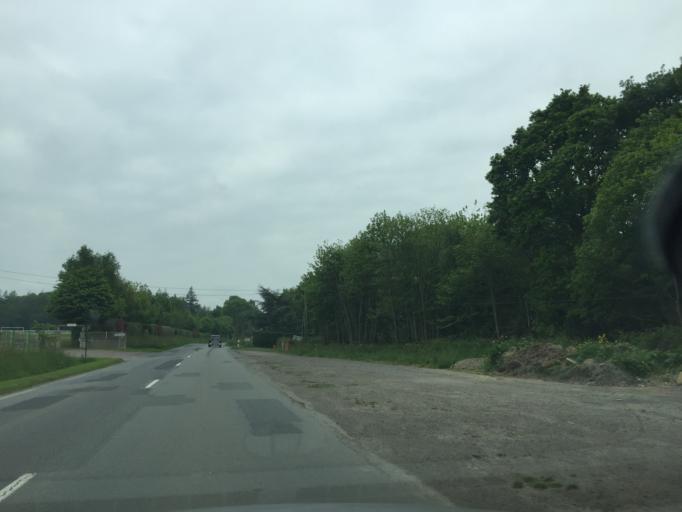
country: FR
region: Brittany
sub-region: Departement des Cotes-d'Armor
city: Henanbihen
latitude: 48.5535
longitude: -2.3840
